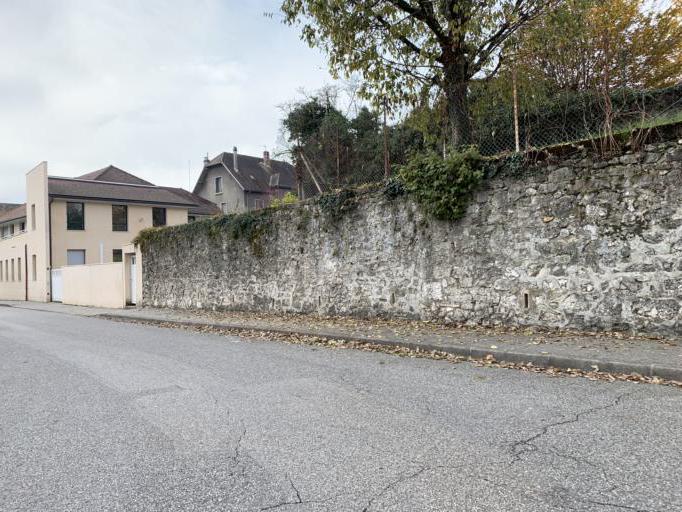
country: FR
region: Rhone-Alpes
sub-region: Departement de l'Ain
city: Belley
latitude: 45.7613
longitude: 5.6890
